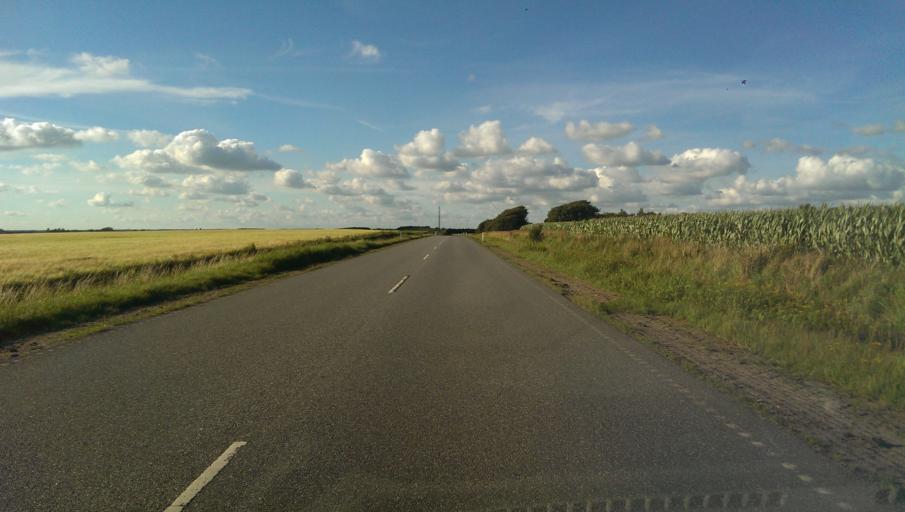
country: DK
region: South Denmark
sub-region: Esbjerg Kommune
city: Tjaereborg
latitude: 55.5121
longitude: 8.5497
